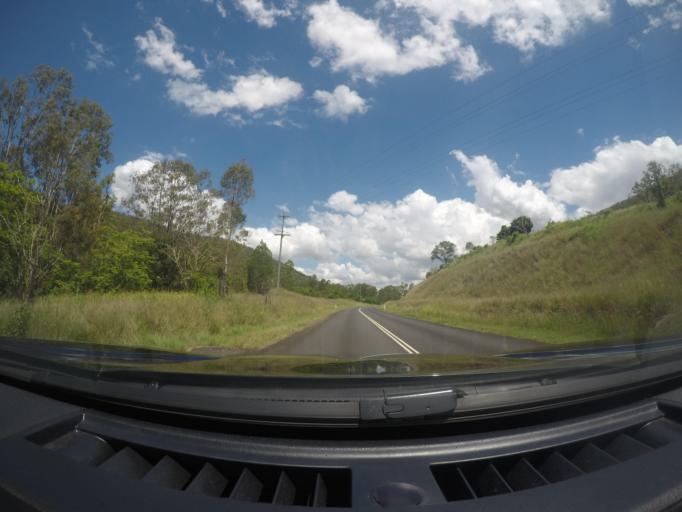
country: AU
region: Queensland
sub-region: Moreton Bay
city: Woodford
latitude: -27.1272
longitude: 152.5519
